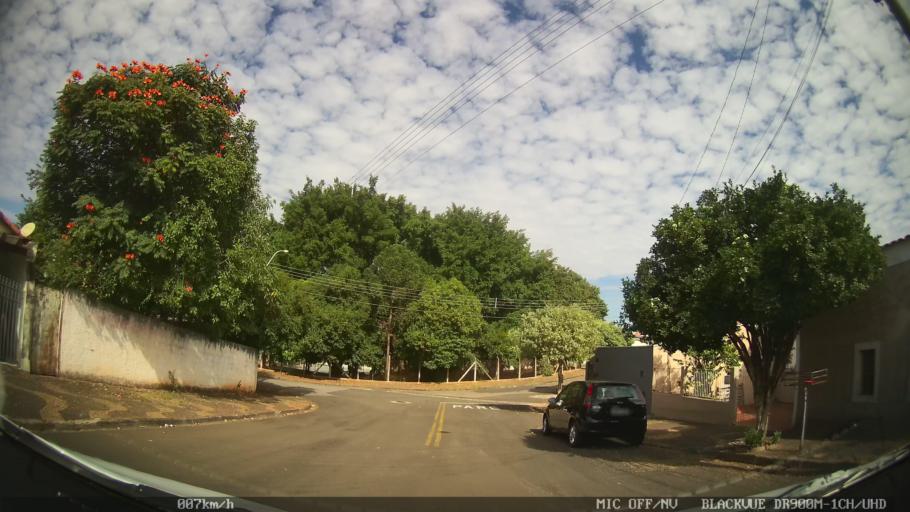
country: BR
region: Sao Paulo
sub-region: Santa Barbara D'Oeste
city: Santa Barbara d'Oeste
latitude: -22.7593
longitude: -47.4216
